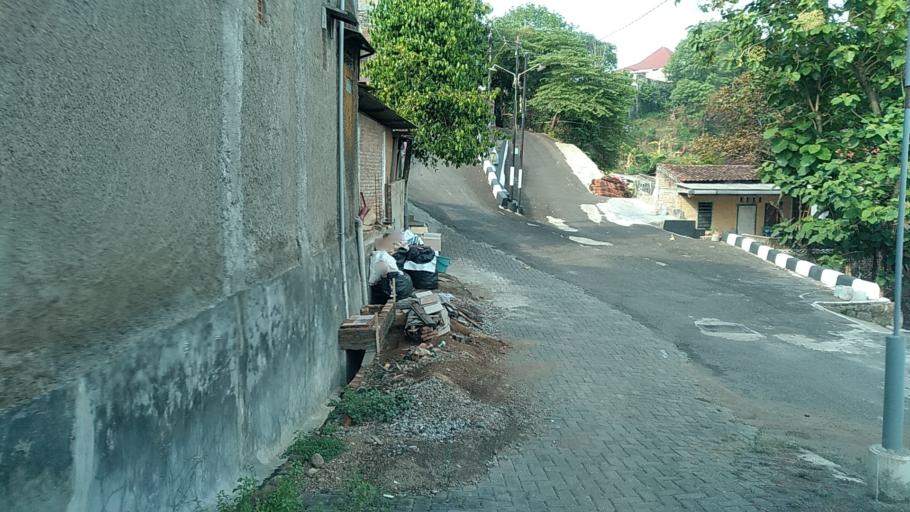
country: ID
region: Central Java
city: Semarang
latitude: -7.0039
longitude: 110.3817
